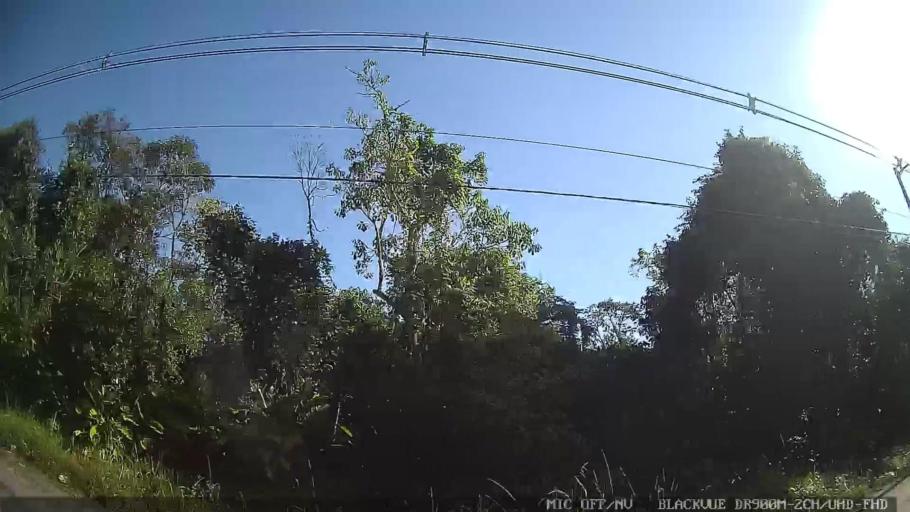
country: BR
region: Sao Paulo
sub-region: Santos
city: Santos
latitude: -23.9033
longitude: -46.3073
